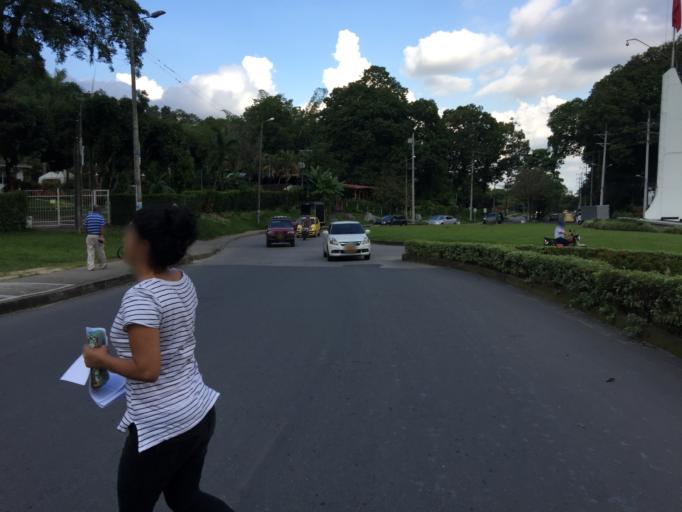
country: CO
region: Tolima
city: Ibague
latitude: 4.4479
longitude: -75.1987
